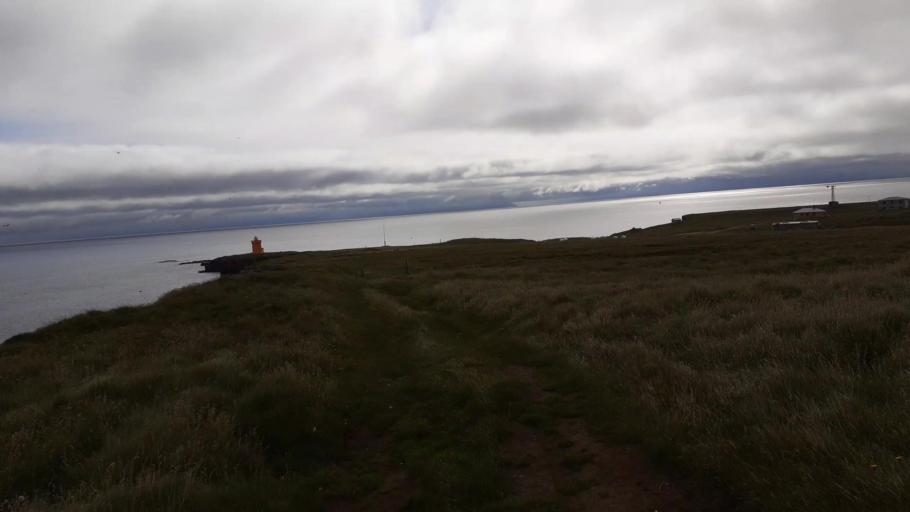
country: IS
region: Northeast
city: Dalvik
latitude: 66.5318
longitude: -17.9818
